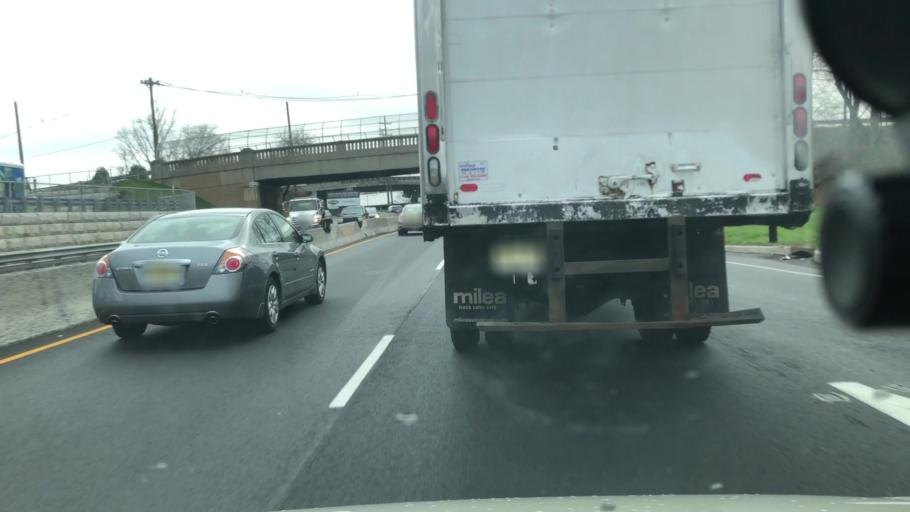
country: US
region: New Jersey
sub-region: Union County
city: Hillside
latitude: 40.6968
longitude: -74.2187
